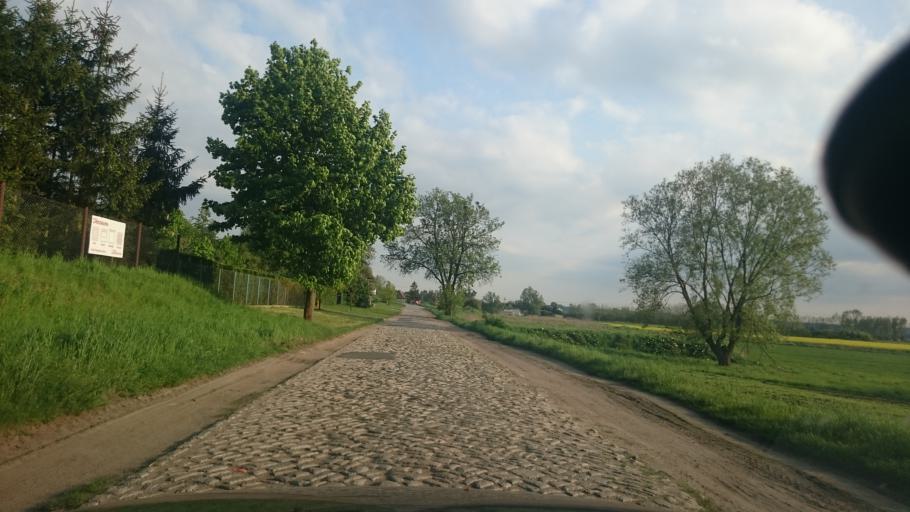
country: PL
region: Kujawsko-Pomorskie
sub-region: Grudziadz
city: Grudziadz
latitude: 53.4716
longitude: 18.8144
